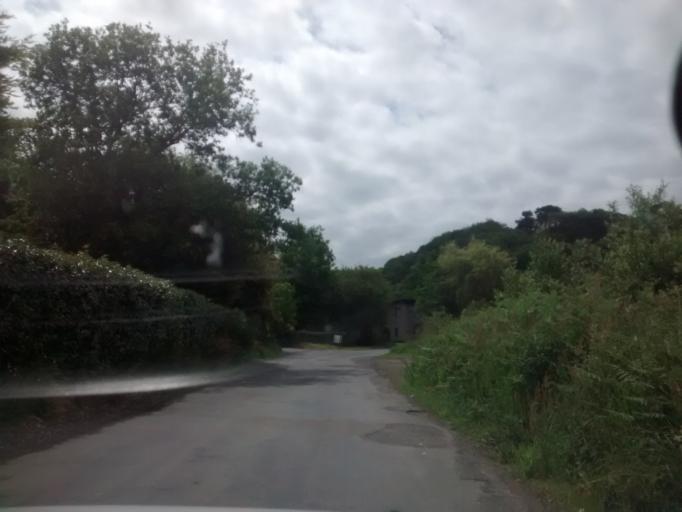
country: FR
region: Brittany
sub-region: Departement des Cotes-d'Armor
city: Trelevern
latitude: 48.8033
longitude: -3.3880
